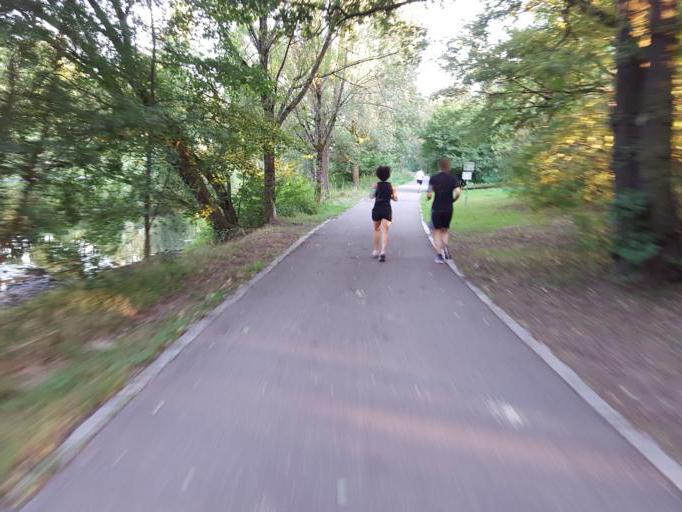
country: DE
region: Baden-Wuerttemberg
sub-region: Karlsruhe Region
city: Karlsruhe
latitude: 48.9975
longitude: 8.3732
